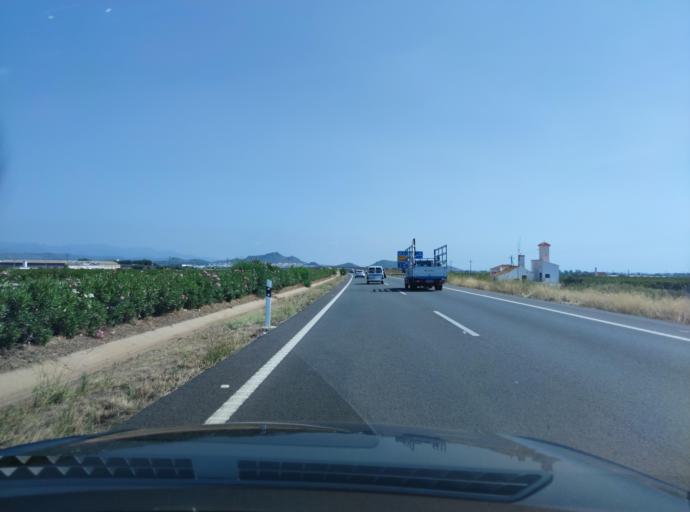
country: ES
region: Valencia
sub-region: Provincia de Valencia
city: Faura
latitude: 39.7118
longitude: -0.2391
